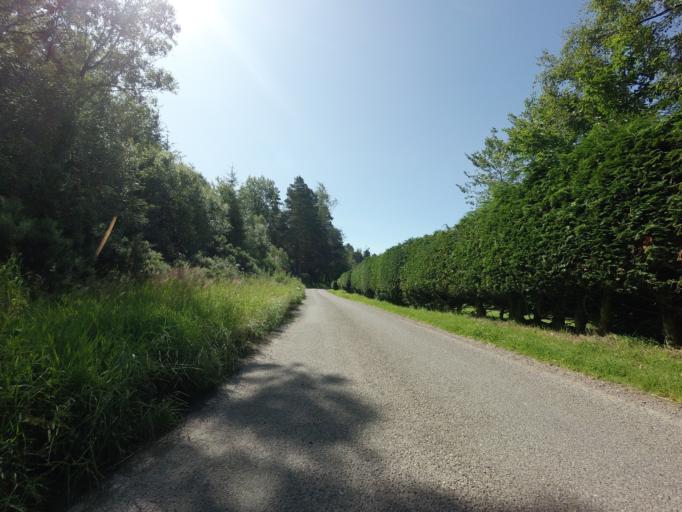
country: GB
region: Scotland
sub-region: Highland
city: Nairn
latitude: 57.5272
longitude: -3.8627
